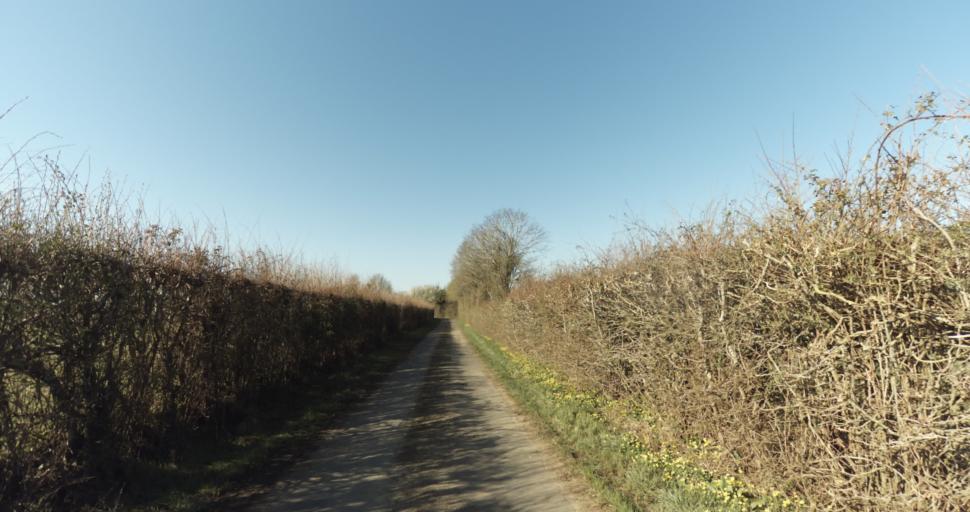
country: FR
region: Lower Normandy
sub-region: Departement du Calvados
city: Saint-Pierre-sur-Dives
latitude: 48.9603
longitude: 0.0202
